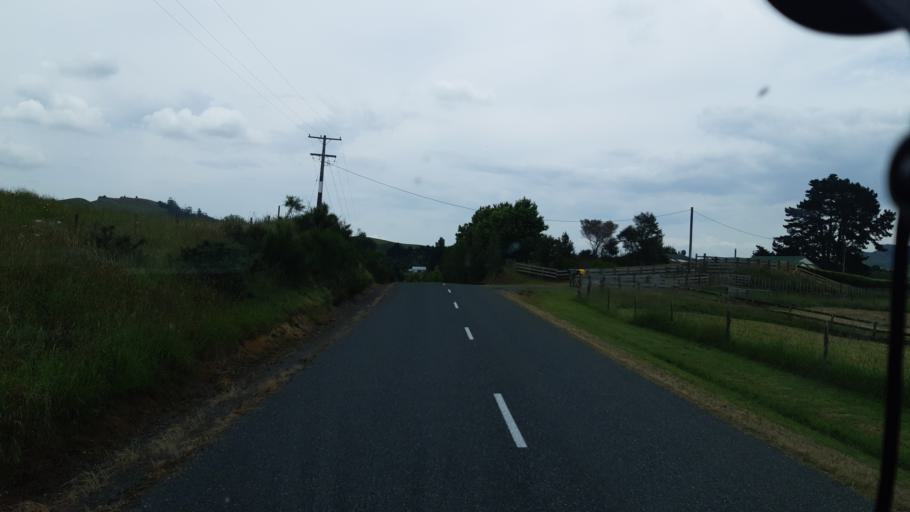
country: NZ
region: Waikato
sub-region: Waikato District
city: Raglan
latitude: -37.8485
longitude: 175.0370
